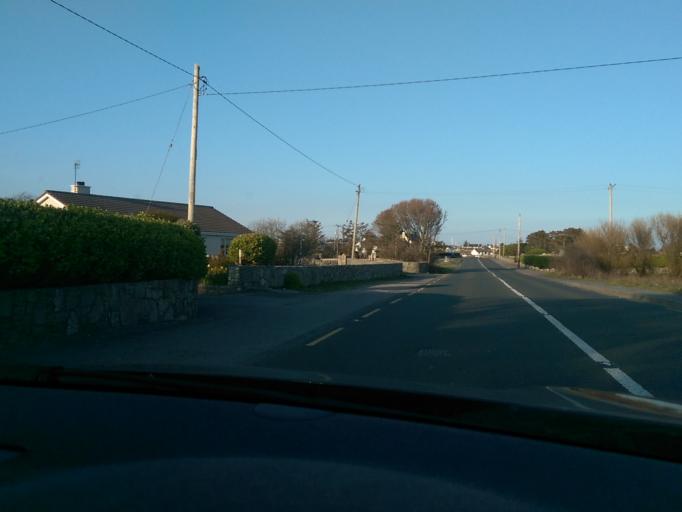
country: IE
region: Connaught
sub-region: County Galway
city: Oughterard
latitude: 53.2397
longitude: -9.4207
